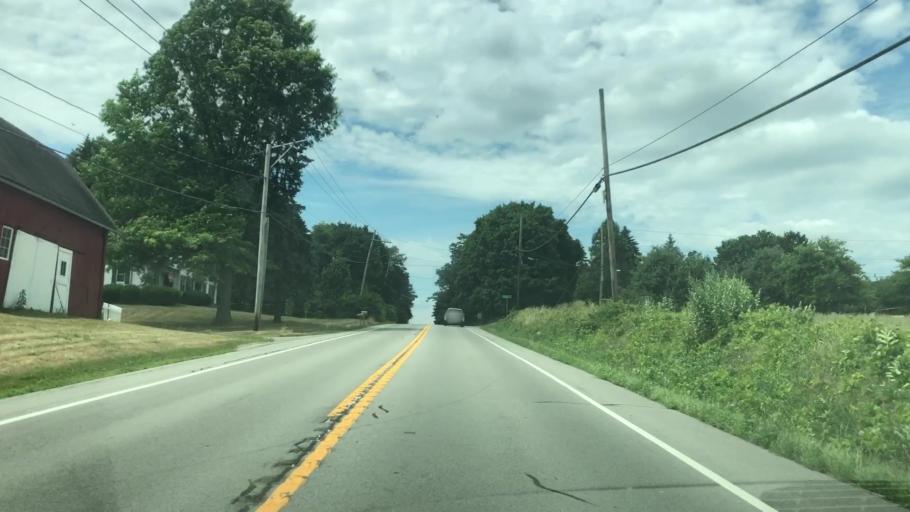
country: US
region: New York
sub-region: Monroe County
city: Fairport
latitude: 43.1307
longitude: -77.3919
